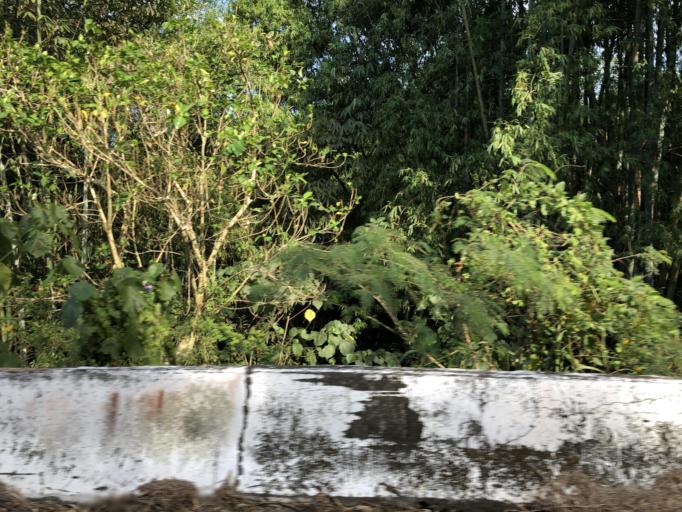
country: TW
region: Taiwan
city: Yujing
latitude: 23.0224
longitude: 120.3968
